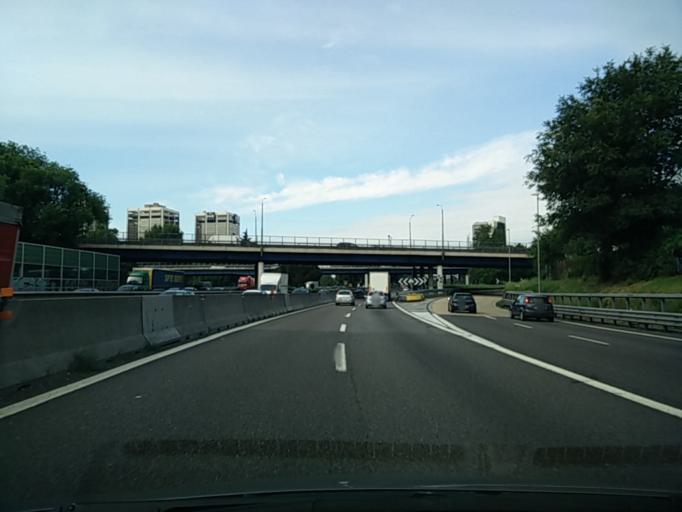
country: IT
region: Lombardy
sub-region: Citta metropolitana di Milano
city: Baranzate
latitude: 45.5166
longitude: 9.1231
